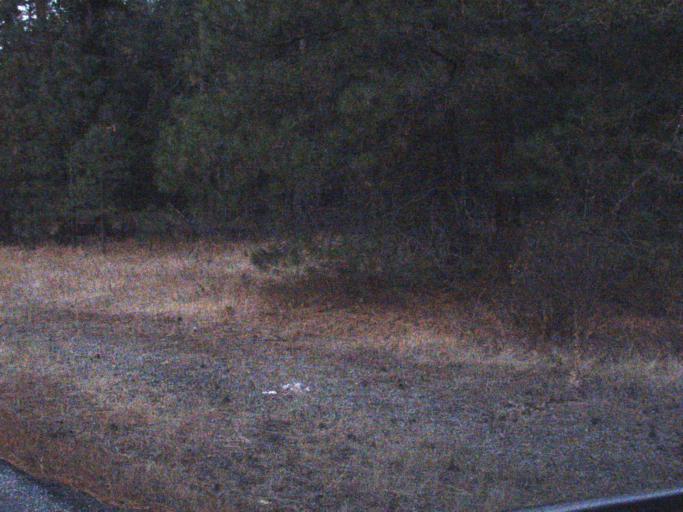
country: US
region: Washington
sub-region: Ferry County
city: Republic
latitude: 48.4703
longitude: -118.7499
